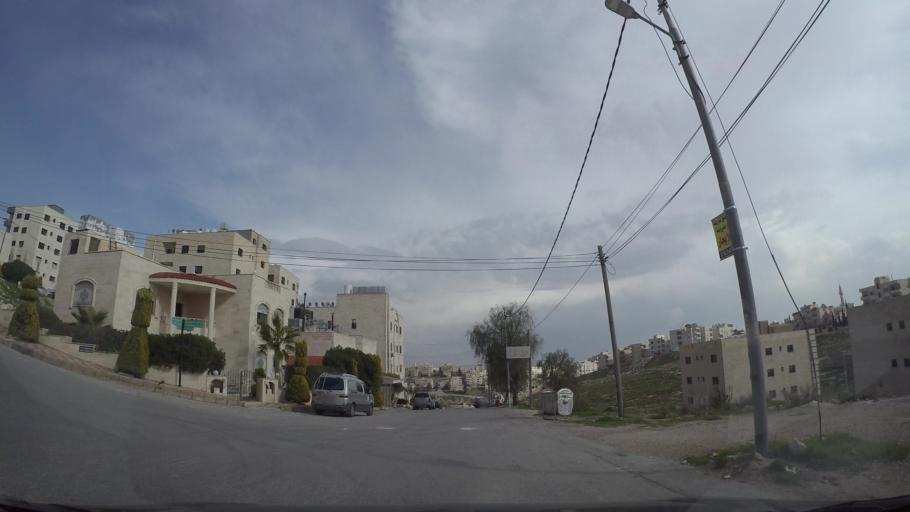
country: JO
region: Amman
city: Amman
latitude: 32.0118
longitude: 35.9413
